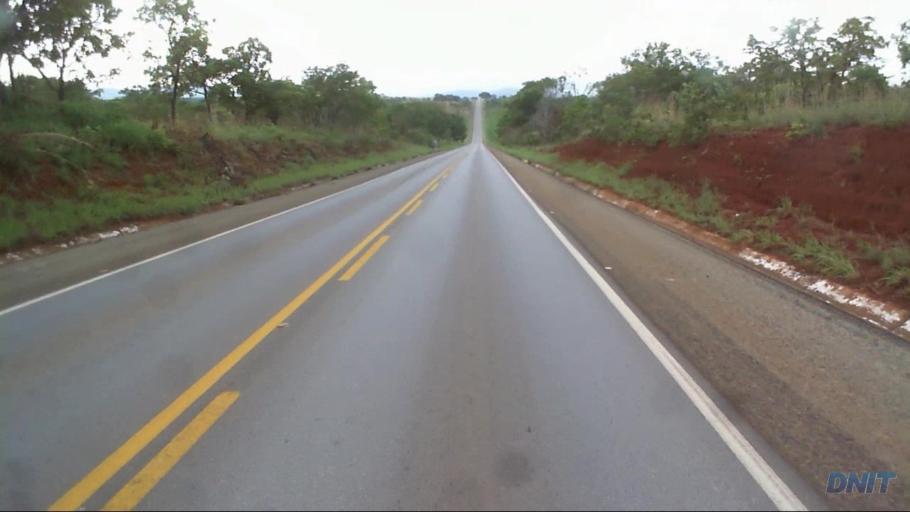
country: BR
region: Goias
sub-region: Barro Alto
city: Barro Alto
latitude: -14.8034
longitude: -49.0474
